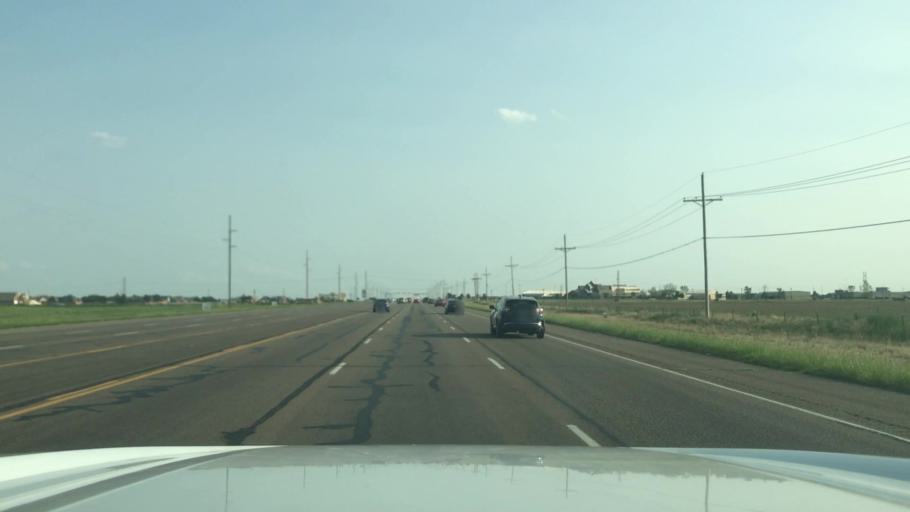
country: US
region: Texas
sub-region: Potter County
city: Amarillo
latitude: 35.1533
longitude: -101.9383
